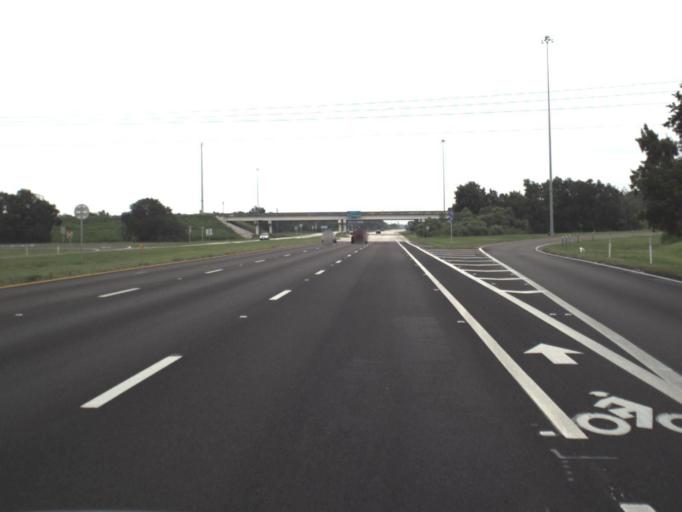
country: US
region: Florida
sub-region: Manatee County
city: Memphis
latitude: 27.5823
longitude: -82.5401
